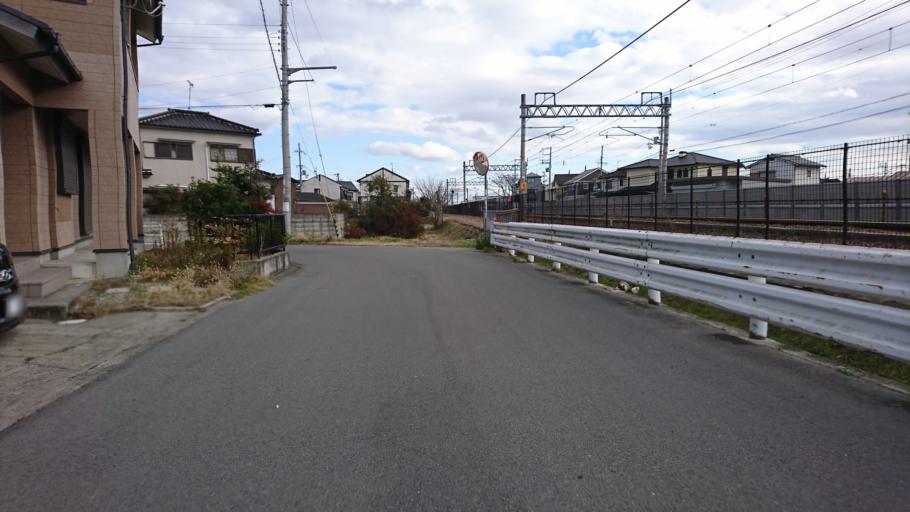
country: JP
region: Hyogo
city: Kakogawacho-honmachi
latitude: 34.7807
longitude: 134.8230
